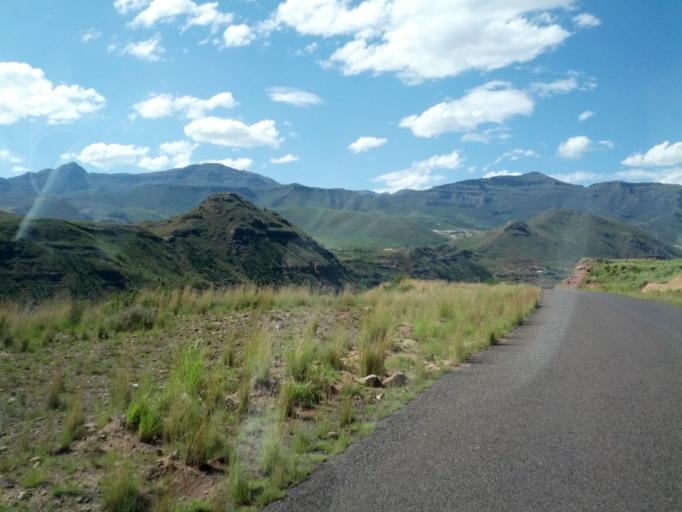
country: LS
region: Qacha's Nek
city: Qacha's Nek
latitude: -30.0659
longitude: 28.4729
